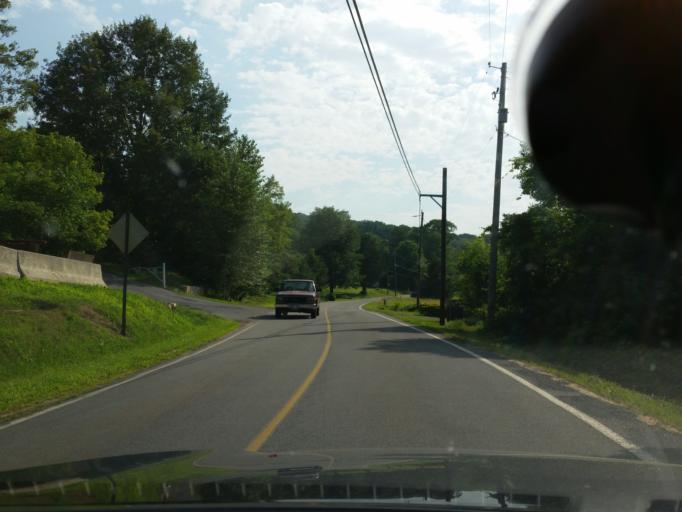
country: US
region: Pennsylvania
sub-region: Perry County
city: Marysville
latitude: 40.3250
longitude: -76.9884
